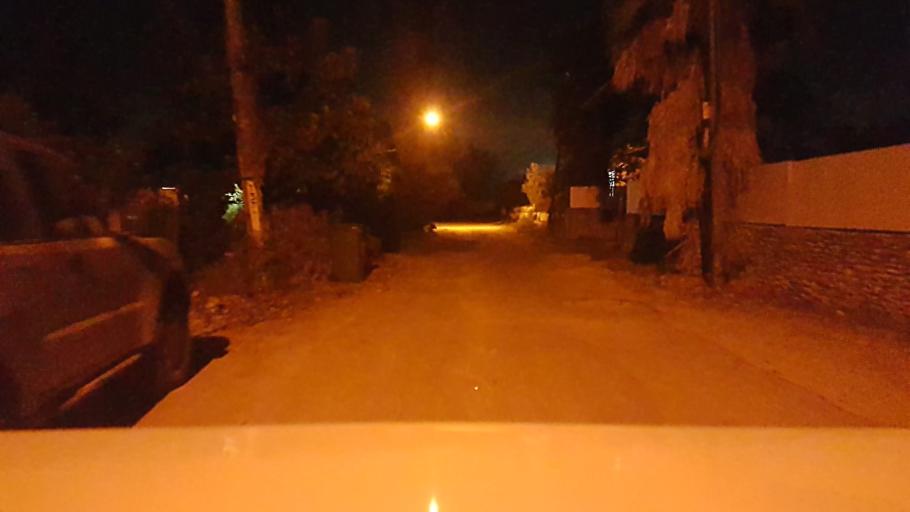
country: IL
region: Central District
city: Nehalim
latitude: 32.0819
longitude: 34.9210
